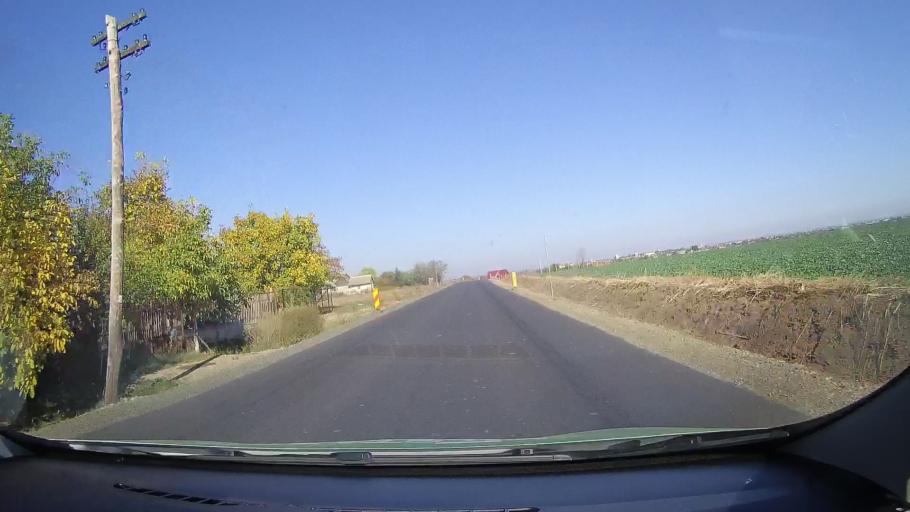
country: RO
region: Satu Mare
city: Carei
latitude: 47.6590
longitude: 22.4599
